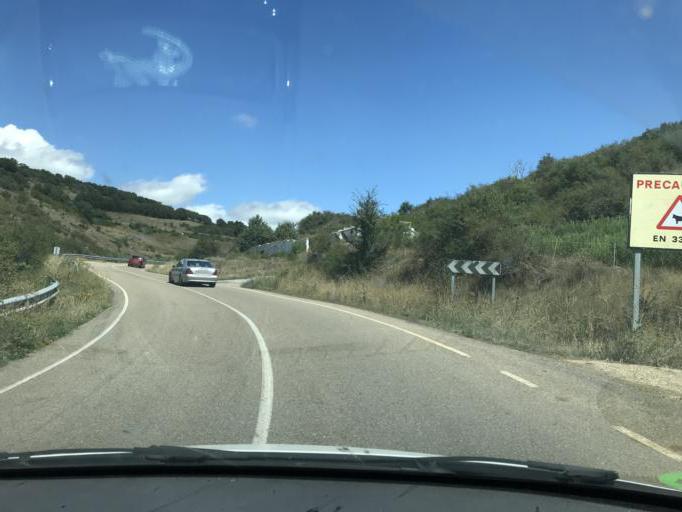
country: ES
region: Castille and Leon
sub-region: Provincia de Palencia
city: Cervera de Pisuerga
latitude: 42.8723
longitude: -4.4951
